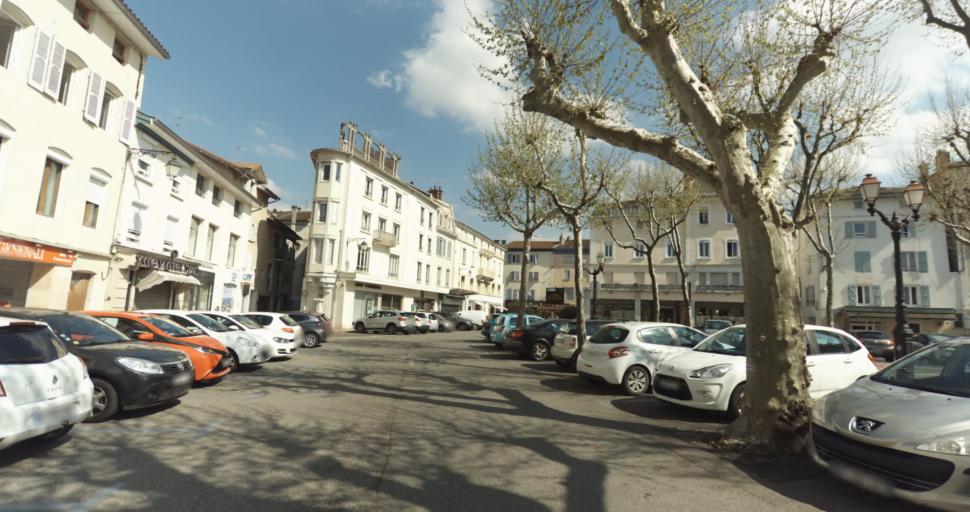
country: FR
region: Rhone-Alpes
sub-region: Departement de l'Isere
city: Saint-Marcellin
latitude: 45.1541
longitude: 5.3206
